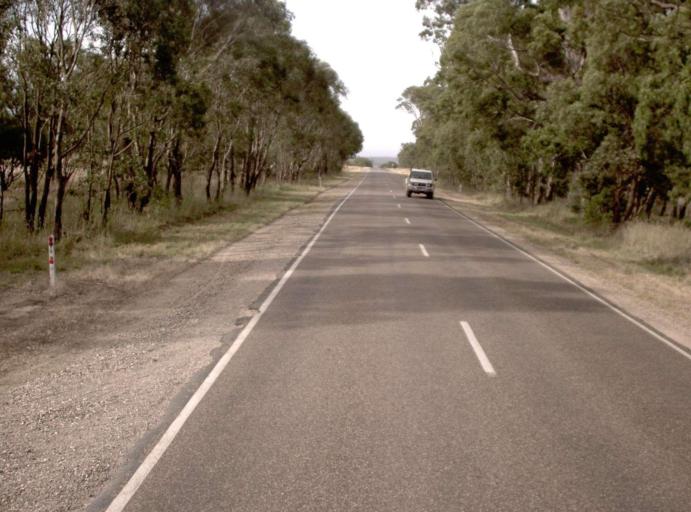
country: AU
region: Victoria
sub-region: Wellington
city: Heyfield
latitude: -38.0291
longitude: 146.6682
